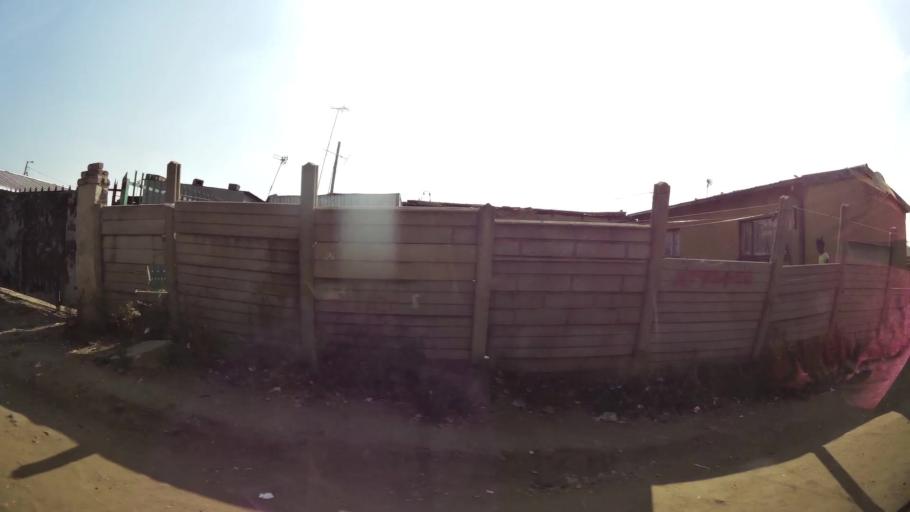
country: ZA
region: Gauteng
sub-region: Ekurhuleni Metropolitan Municipality
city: Brakpan
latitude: -26.1419
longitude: 28.4192
